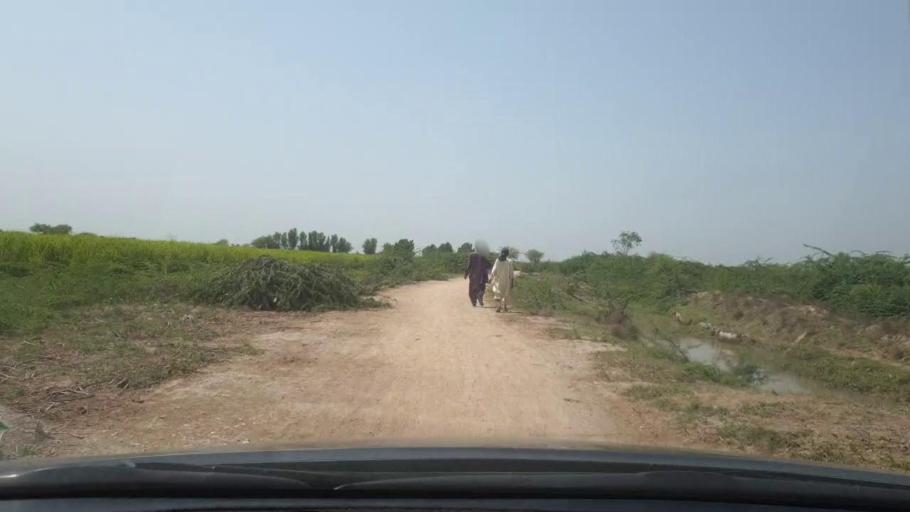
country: PK
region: Sindh
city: Tando Bago
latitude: 24.7747
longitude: 69.1817
